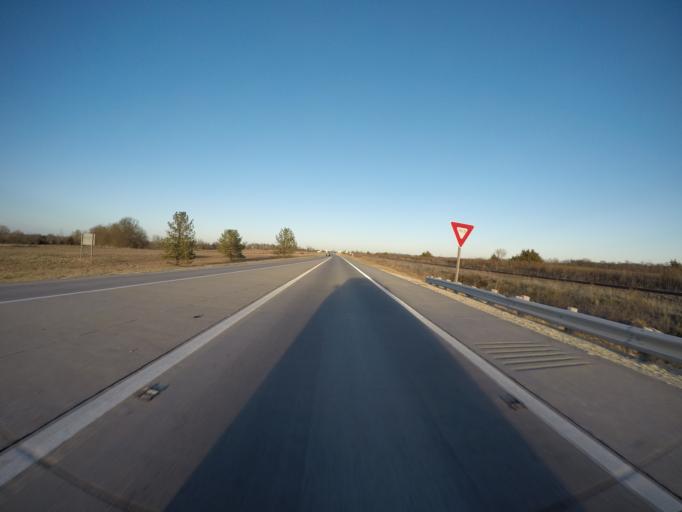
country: US
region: Kansas
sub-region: Harvey County
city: North Newton
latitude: 38.0676
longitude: -97.3097
